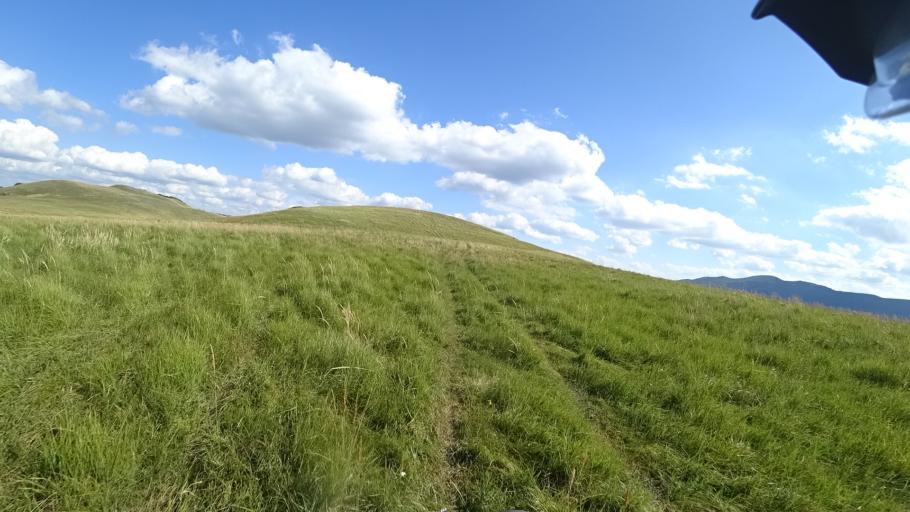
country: HR
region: Zadarska
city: Gracac
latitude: 44.3897
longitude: 16.0270
